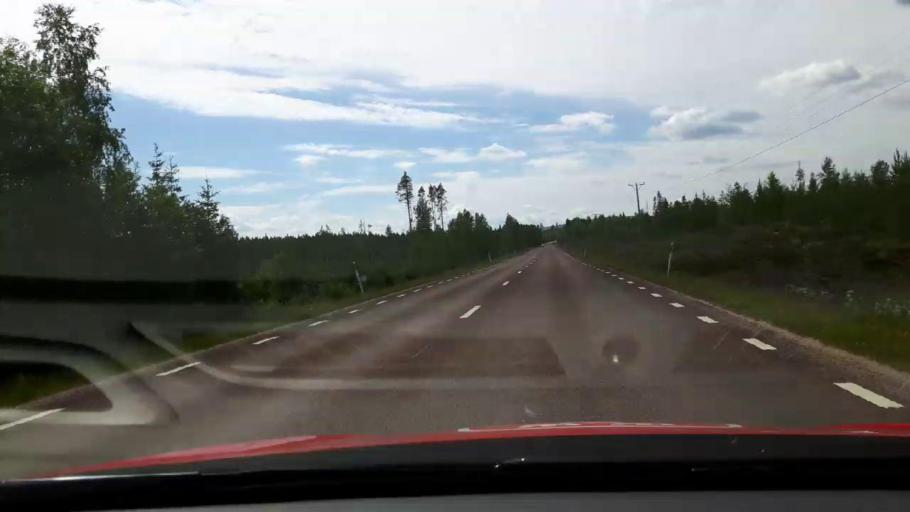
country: SE
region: Jaemtland
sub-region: Harjedalens Kommun
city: Sveg
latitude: 62.0589
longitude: 14.9097
